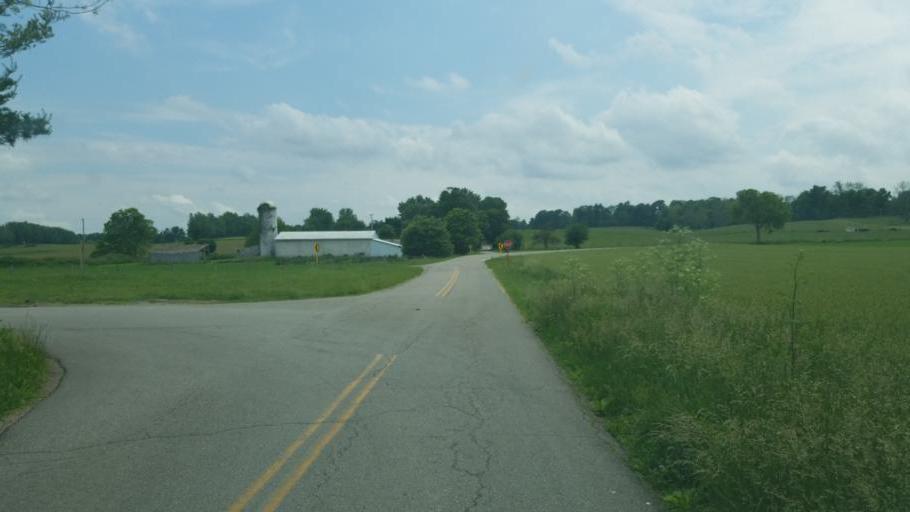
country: US
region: Ohio
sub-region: Perry County
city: Thornport
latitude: 39.9010
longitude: -82.3909
